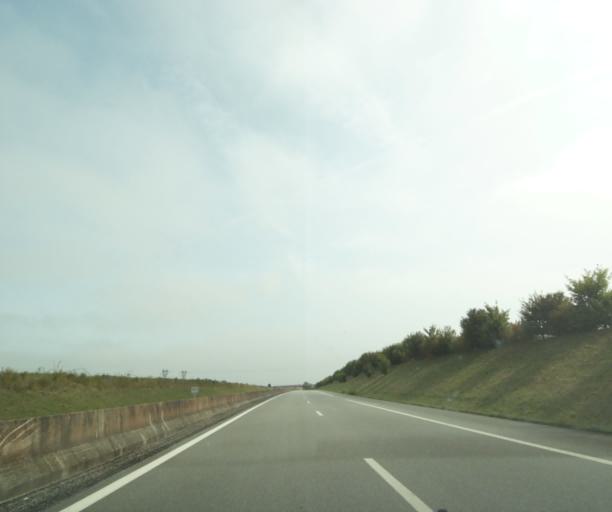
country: FR
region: Lower Normandy
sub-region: Departement de l'Orne
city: Sees
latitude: 48.5939
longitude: 0.1888
